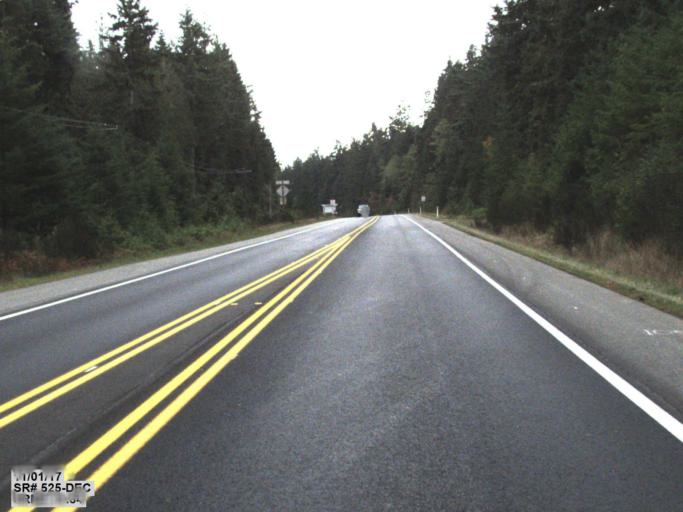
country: US
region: Washington
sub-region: Island County
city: Langley
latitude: 47.9881
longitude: -122.3936
